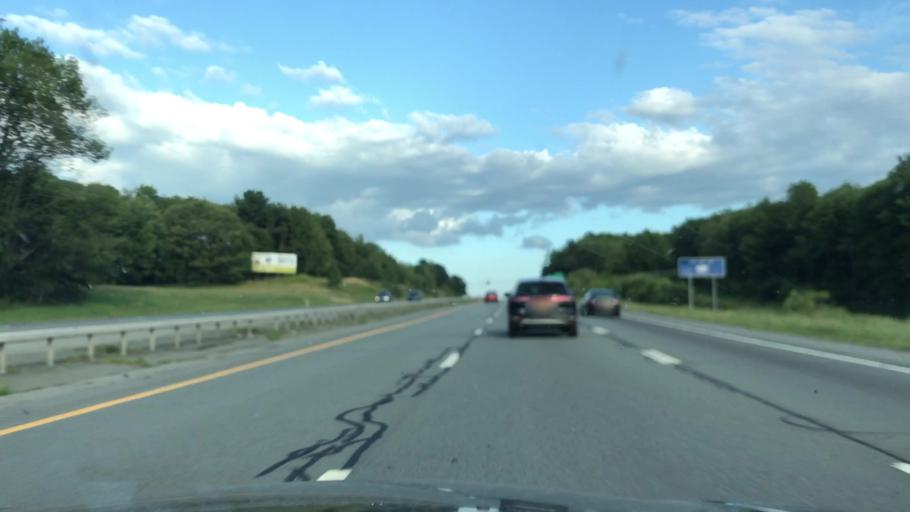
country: US
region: New York
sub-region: Sullivan County
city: Rock Hill
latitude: 41.6285
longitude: -74.6070
